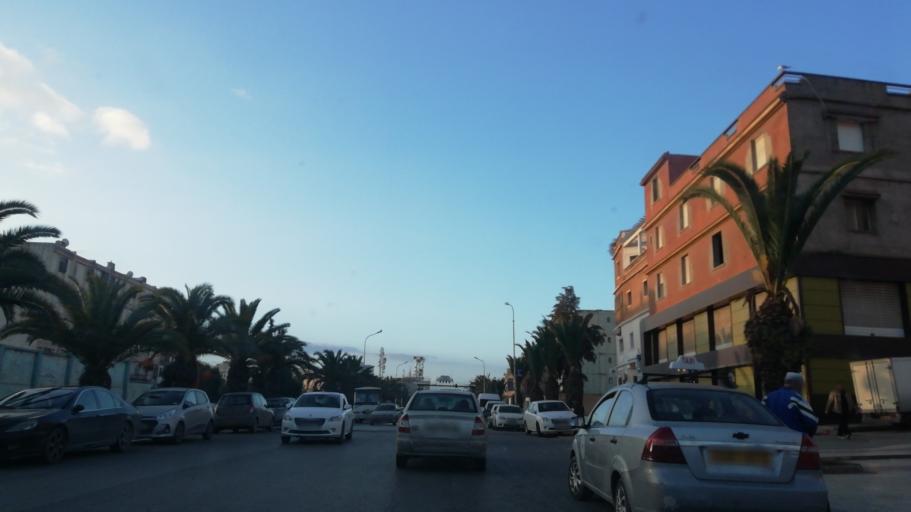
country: DZ
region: Oran
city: Oran
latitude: 35.6735
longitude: -0.6579
